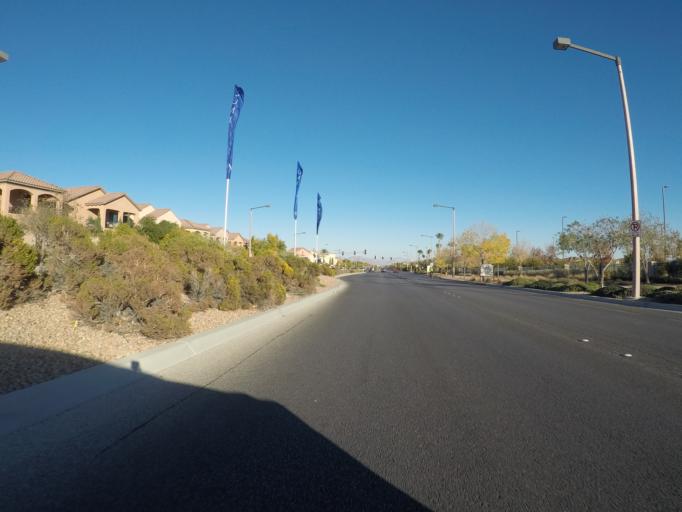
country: US
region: Nevada
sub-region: Clark County
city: Summerlin South
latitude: 36.1589
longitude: -115.3539
